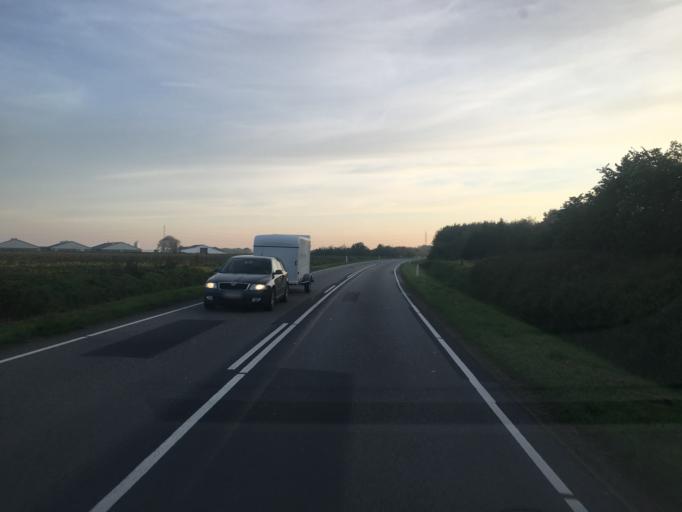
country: DK
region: South Denmark
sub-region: Tonder Kommune
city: Logumkloster
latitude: 55.0465
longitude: 9.0928
